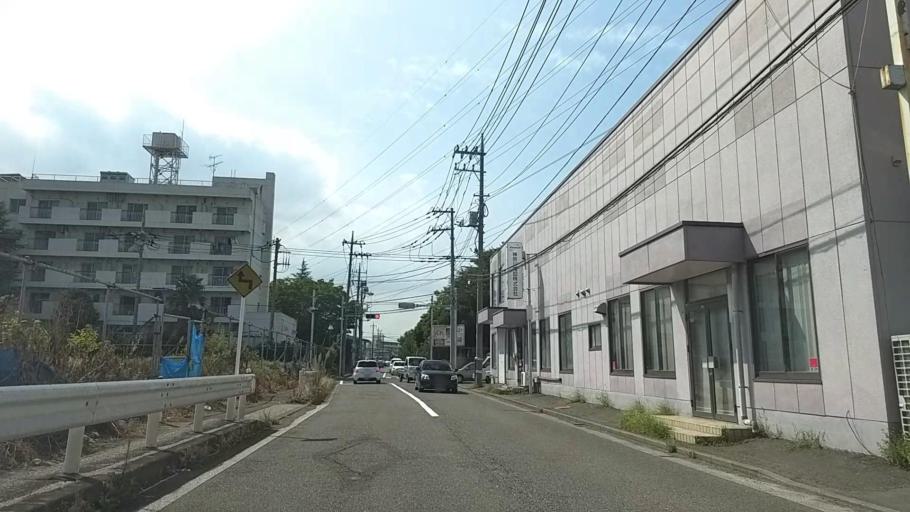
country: JP
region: Kanagawa
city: Yokohama
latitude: 35.5168
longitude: 139.5840
